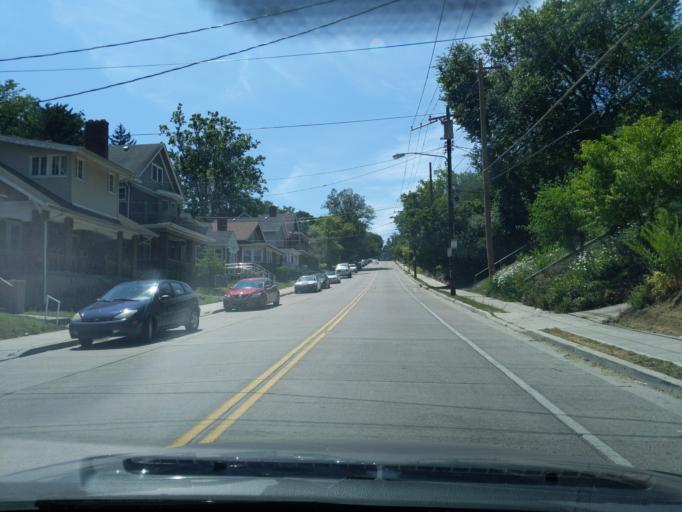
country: US
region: Ohio
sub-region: Hamilton County
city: Saint Bernard
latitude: 39.1499
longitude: -84.5132
